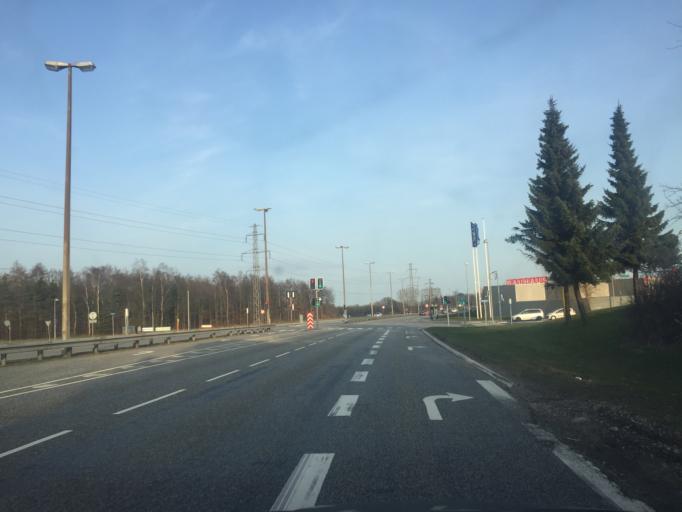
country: DK
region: Capital Region
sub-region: Ishoj Kommune
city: Ishoj
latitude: 55.6221
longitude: 12.3352
